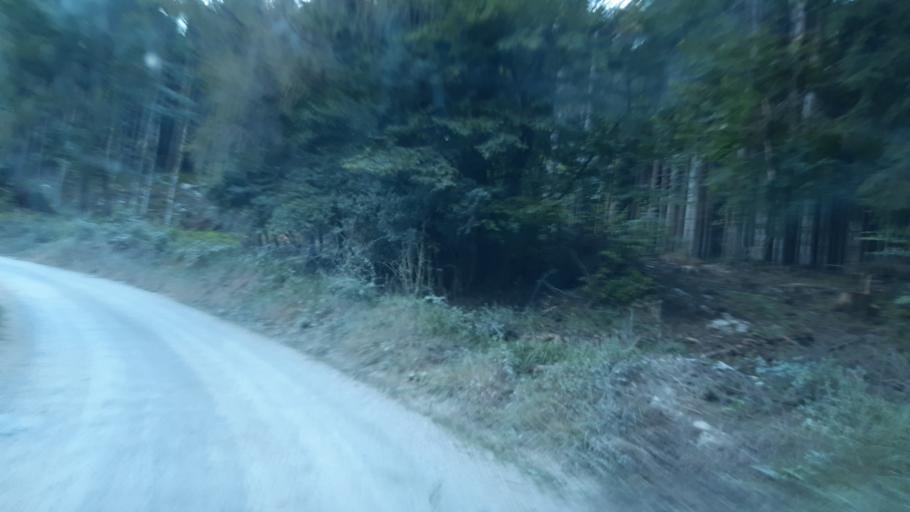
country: SI
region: Dolenjske Toplice
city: Dolenjske Toplice
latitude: 45.7166
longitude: 15.0133
